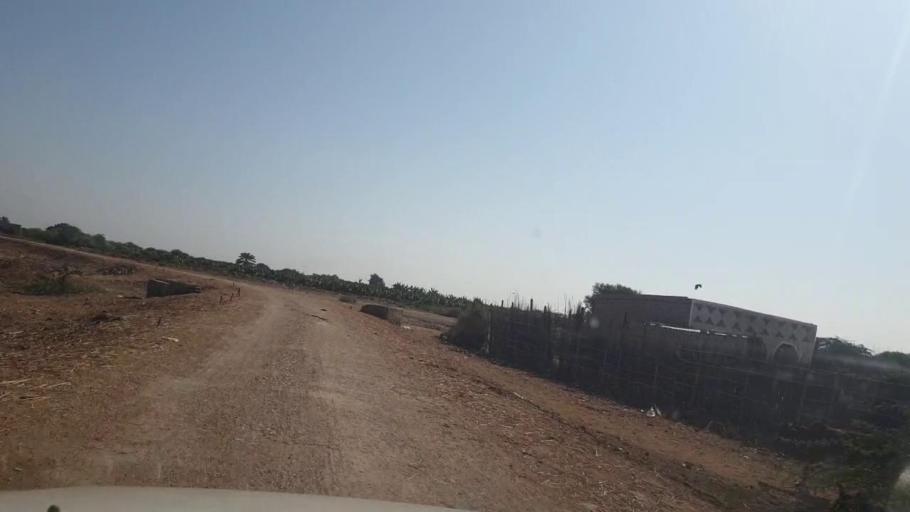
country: PK
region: Sindh
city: Chuhar Jamali
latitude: 24.4500
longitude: 67.8671
